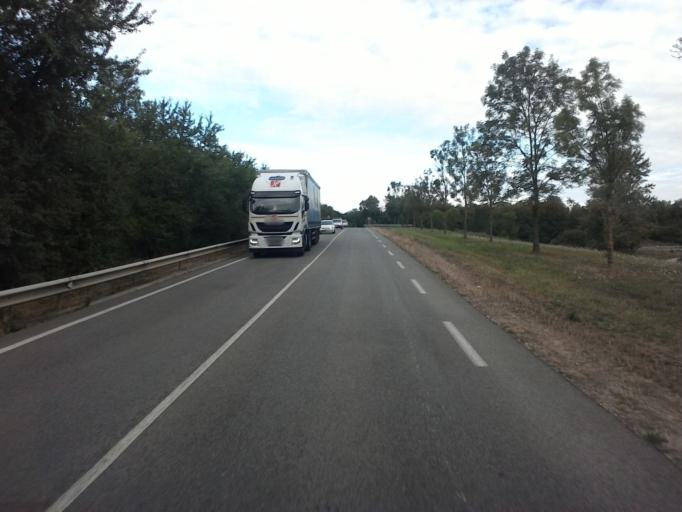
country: FR
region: Rhone-Alpes
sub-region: Departement de l'Ain
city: Saint-Martin-du-Mont
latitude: 46.0663
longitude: 5.3298
